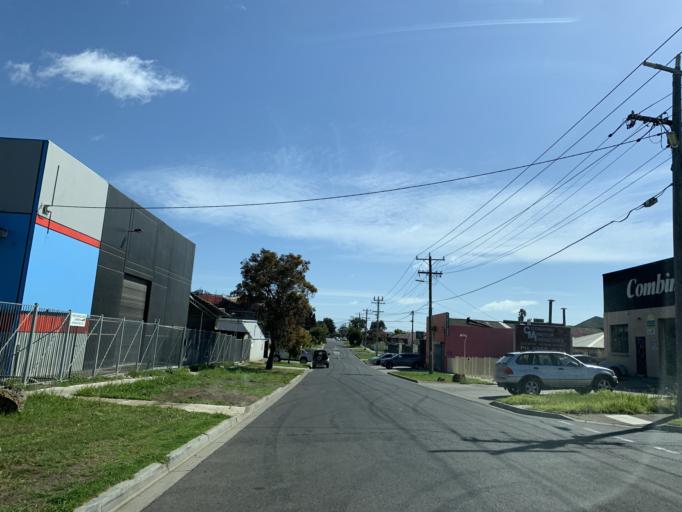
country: AU
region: Victoria
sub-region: Brimbank
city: Saint Albans
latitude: -37.7352
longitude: 144.7963
